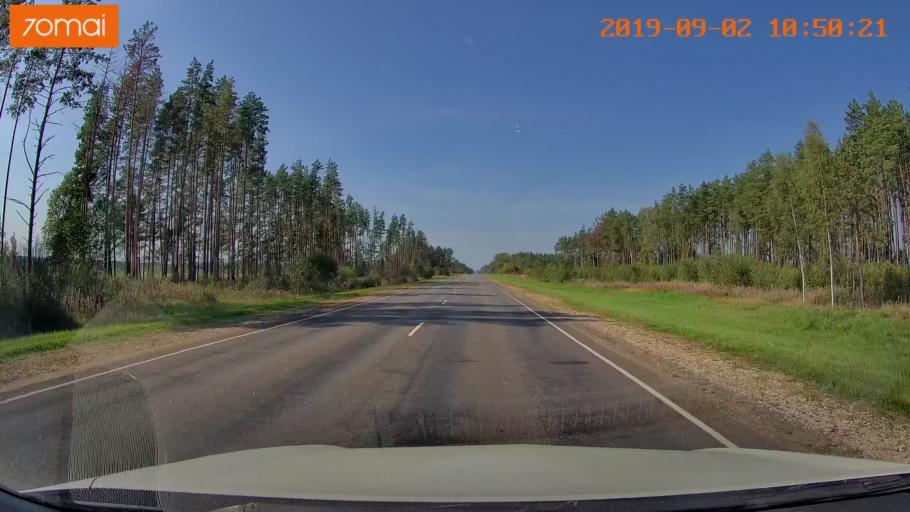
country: RU
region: Smolensk
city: Yekimovichi
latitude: 54.2187
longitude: 33.6442
